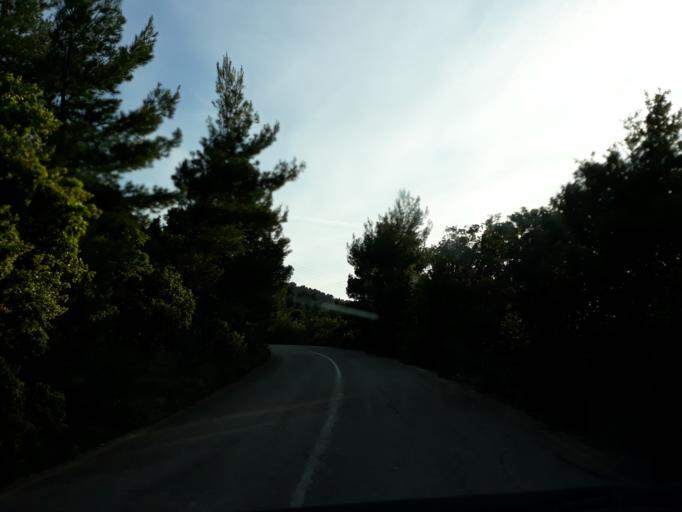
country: GR
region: Attica
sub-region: Nomarchia Anatolikis Attikis
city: Afidnes
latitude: 38.2264
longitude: 23.7926
